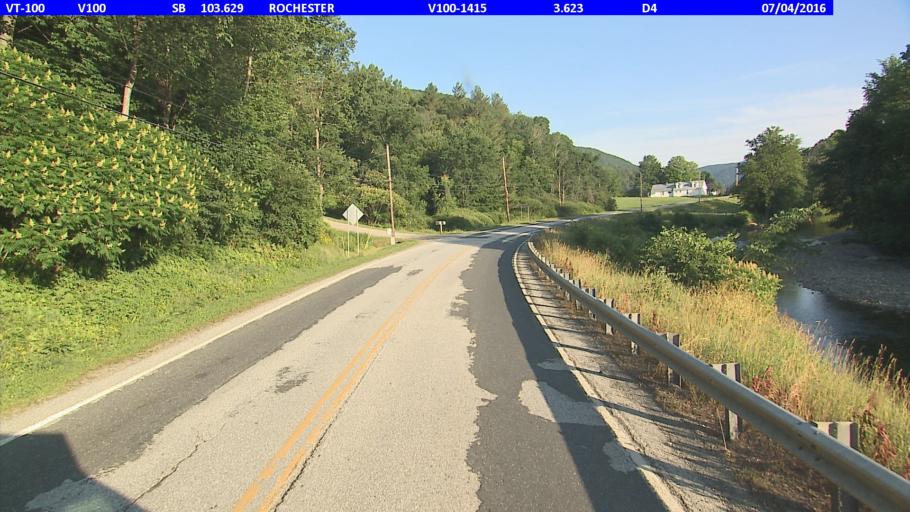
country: US
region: Vermont
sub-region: Orange County
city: Randolph
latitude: 43.8536
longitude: -72.8017
